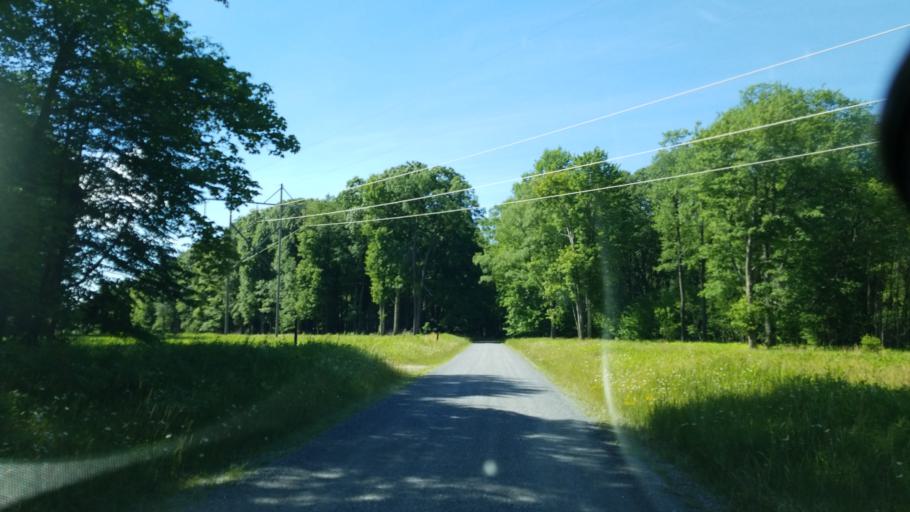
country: US
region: Pennsylvania
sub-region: Clearfield County
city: Clearfield
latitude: 41.1935
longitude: -78.4819
